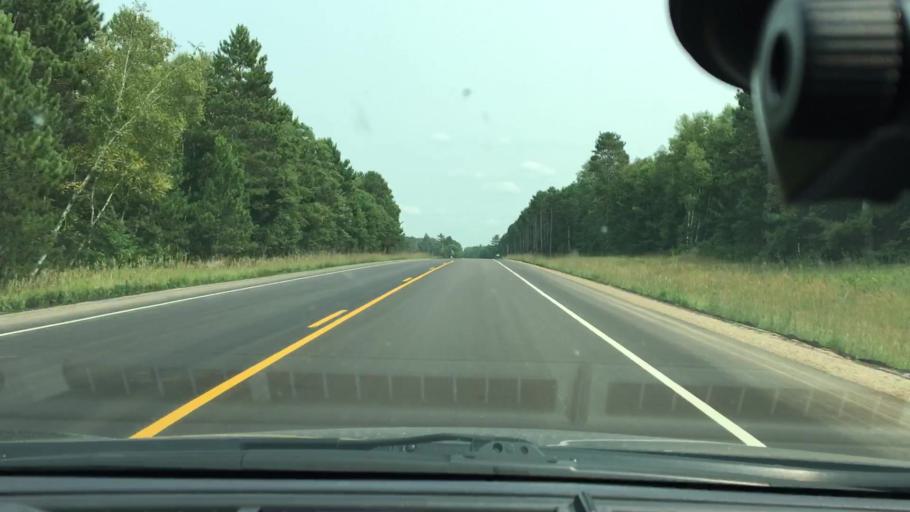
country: US
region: Minnesota
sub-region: Crow Wing County
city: Nisswa
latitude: 46.5292
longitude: -94.2559
